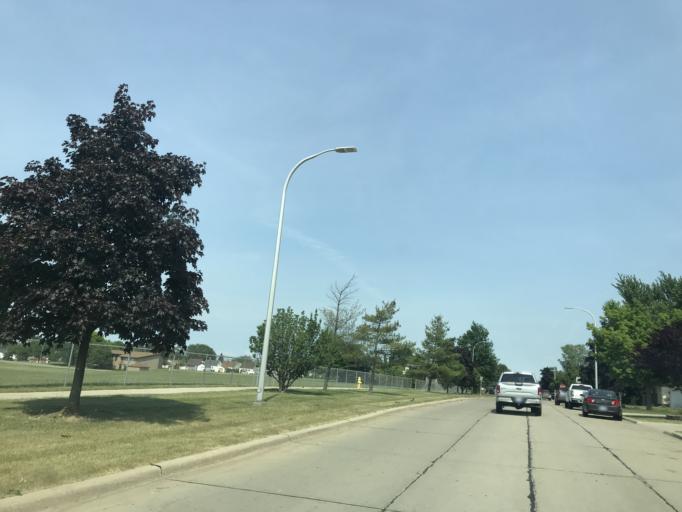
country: US
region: Michigan
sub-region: Wayne County
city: Riverview
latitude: 42.1776
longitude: -83.1877
